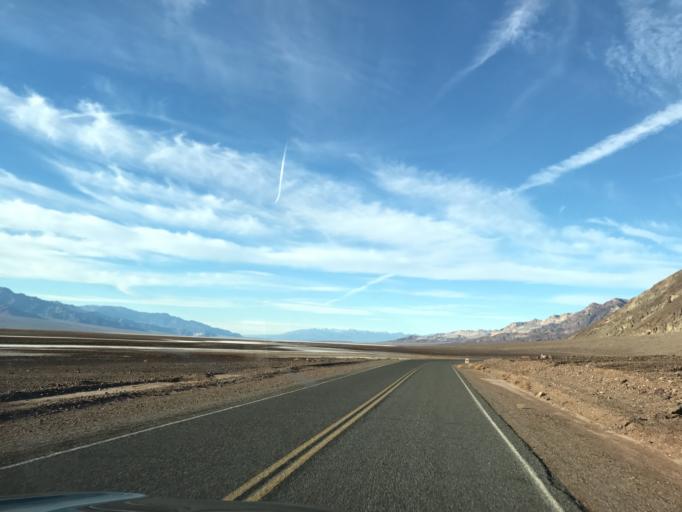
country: US
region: Nevada
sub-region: Nye County
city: Beatty
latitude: 36.1936
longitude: -116.7724
